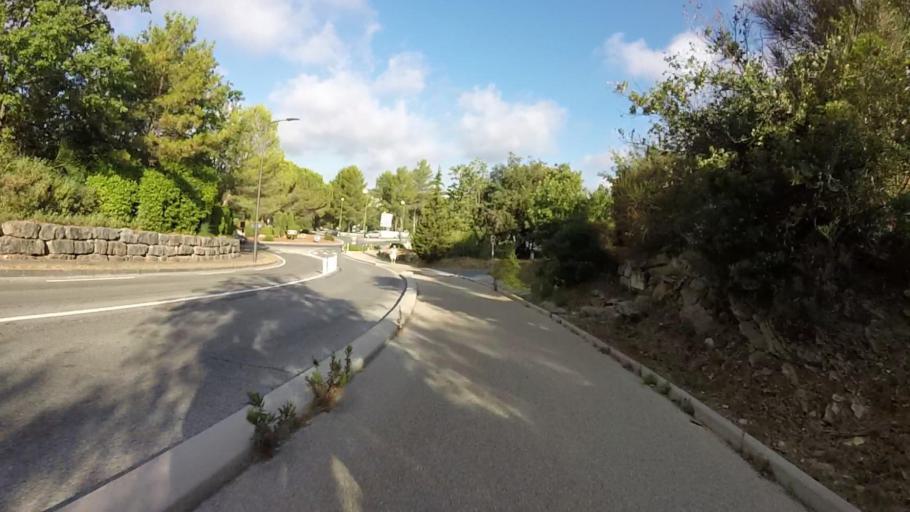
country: FR
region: Provence-Alpes-Cote d'Azur
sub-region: Departement des Alpes-Maritimes
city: Biot
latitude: 43.6248
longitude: 7.0578
